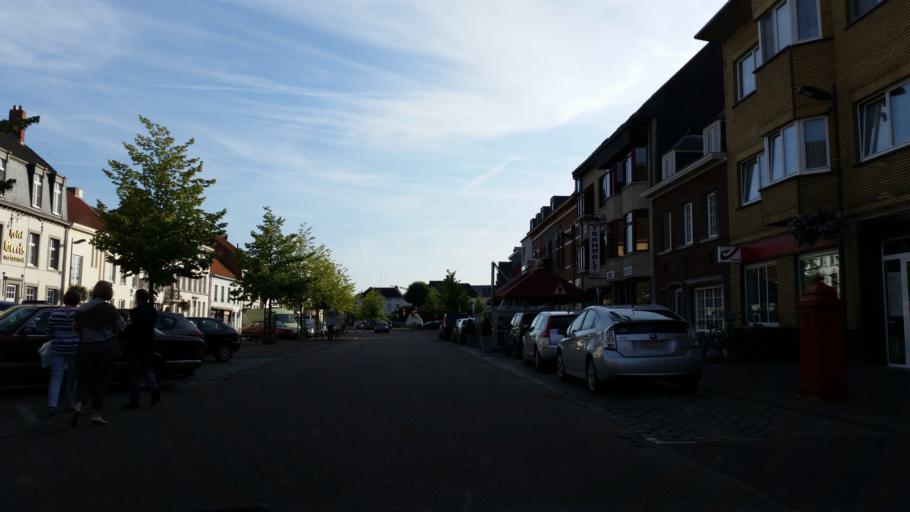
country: BE
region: Flanders
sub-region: Provincie Antwerpen
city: Westerlo
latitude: 51.0879
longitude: 4.9187
